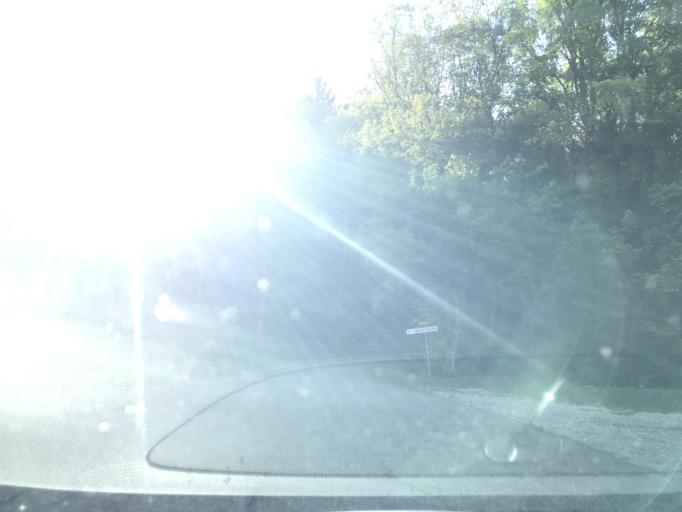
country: FR
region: Rhone-Alpes
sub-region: Departement de la Savoie
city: Novalaise
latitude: 45.6443
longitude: 5.7992
